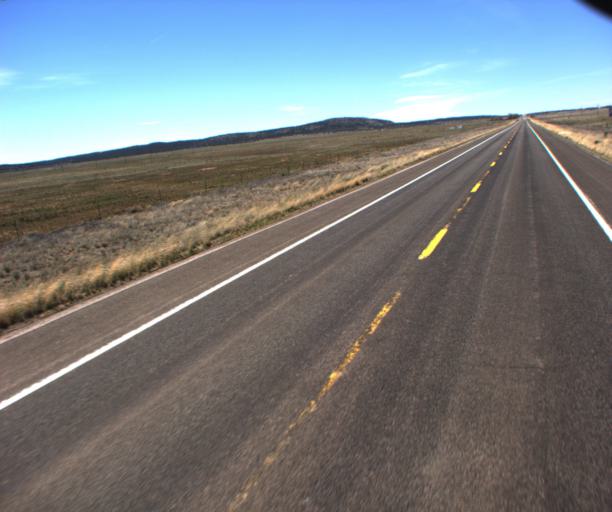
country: US
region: Arizona
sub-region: Mohave County
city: Peach Springs
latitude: 35.4689
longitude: -113.1228
